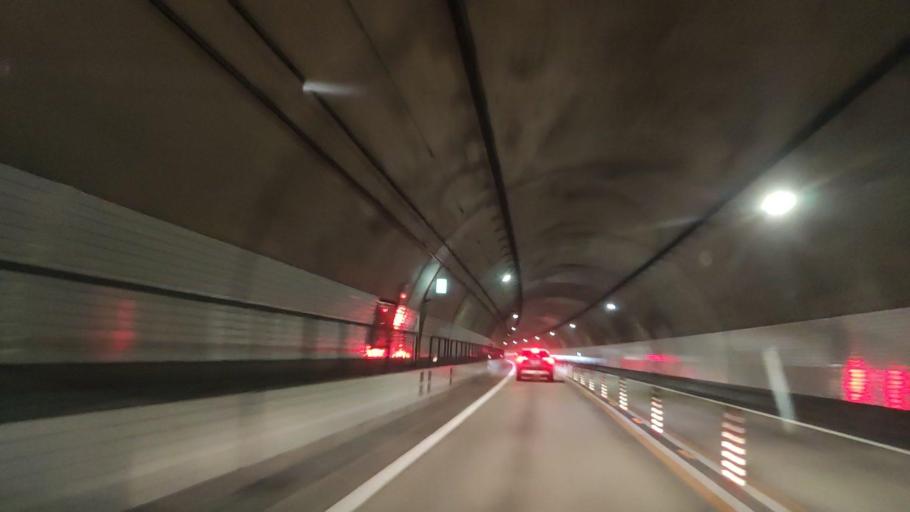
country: JP
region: Kyoto
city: Miyazu
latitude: 35.5584
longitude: 135.1241
